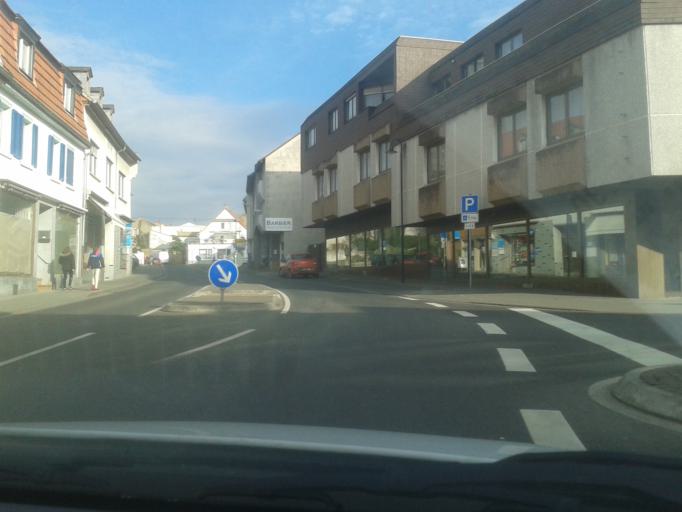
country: DE
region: Rheinland-Pfalz
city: Ingelheim am Rhein
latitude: 49.9757
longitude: 8.0642
